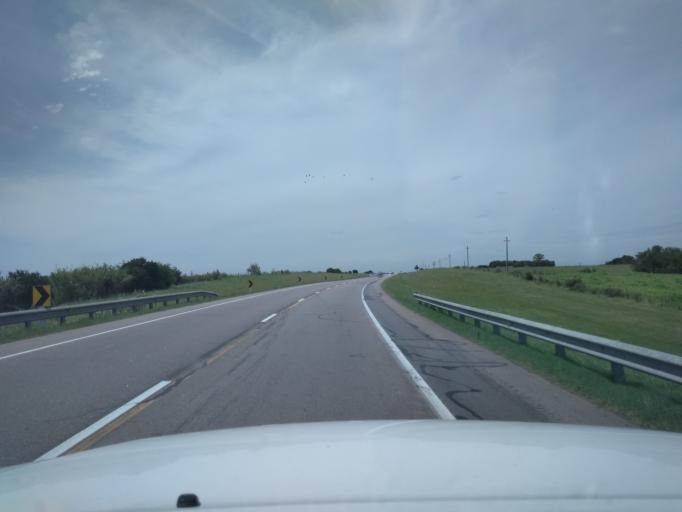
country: UY
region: Florida
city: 25 de Mayo
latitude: -34.2318
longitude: -56.2130
